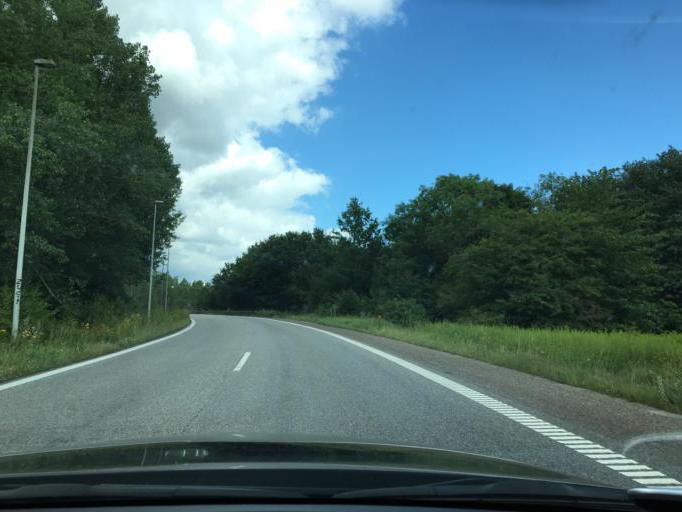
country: DK
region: Capital Region
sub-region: Brondby Kommune
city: Brondbyvester
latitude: 55.6417
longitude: 12.4266
